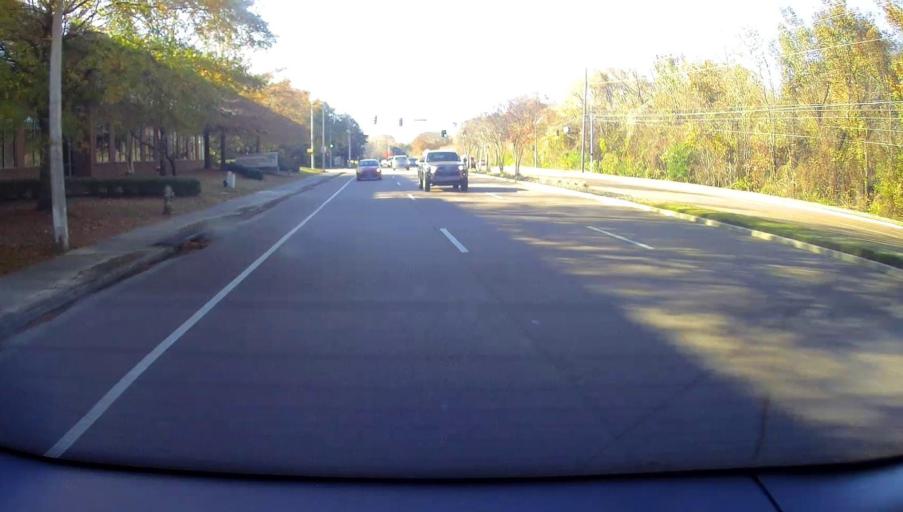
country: US
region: Tennessee
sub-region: Shelby County
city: Germantown
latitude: 35.1161
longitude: -89.8222
